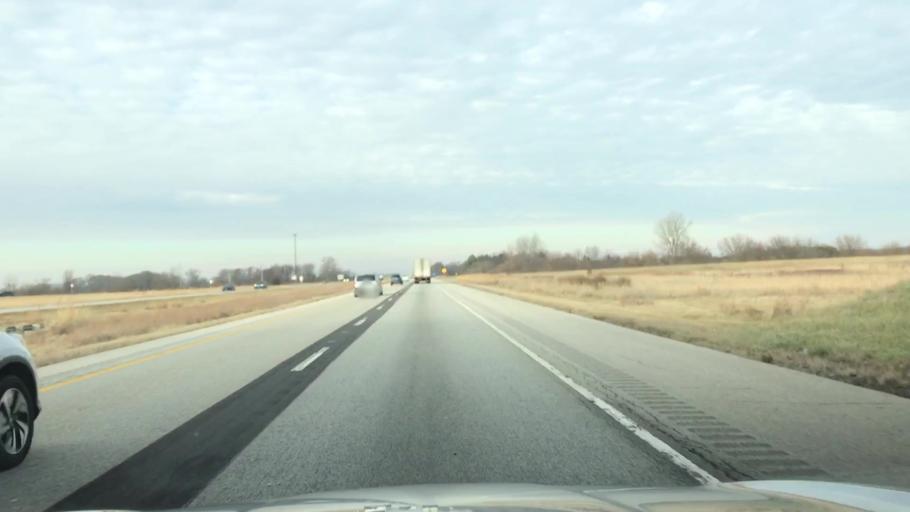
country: US
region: Illinois
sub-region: Sangamon County
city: Divernon
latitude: 39.5680
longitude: -89.6460
